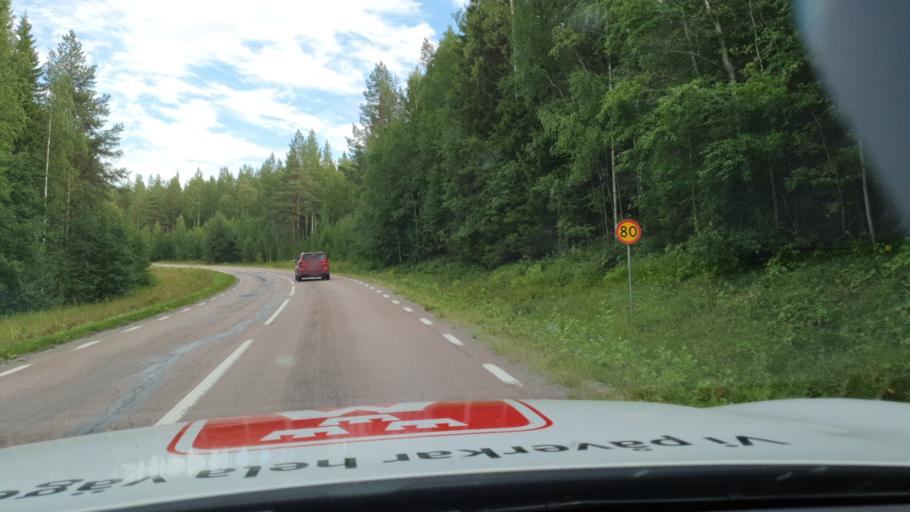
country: SE
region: Jaemtland
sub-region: Stroemsunds Kommun
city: Stroemsund
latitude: 63.6271
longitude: 16.0713
